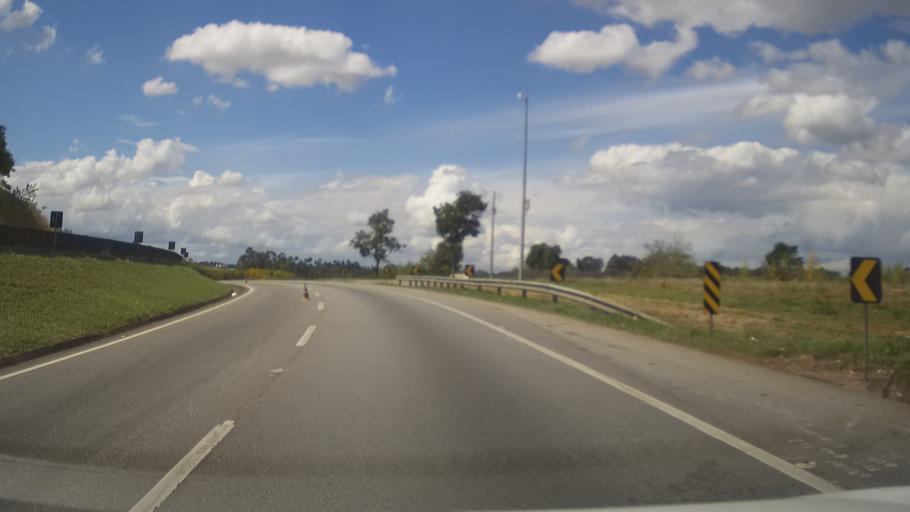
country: BR
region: Minas Gerais
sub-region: Oliveira
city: Oliveira
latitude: -20.8387
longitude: -44.8241
